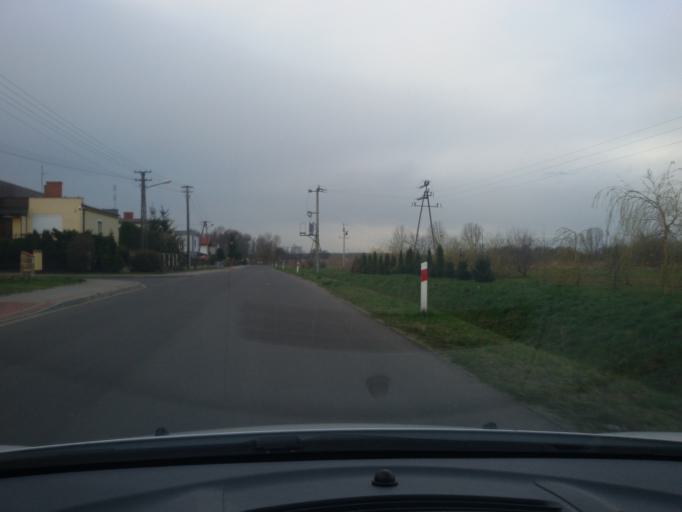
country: PL
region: Greater Poland Voivodeship
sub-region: Powiat gostynski
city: Krobia
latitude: 51.7677
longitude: 16.9291
